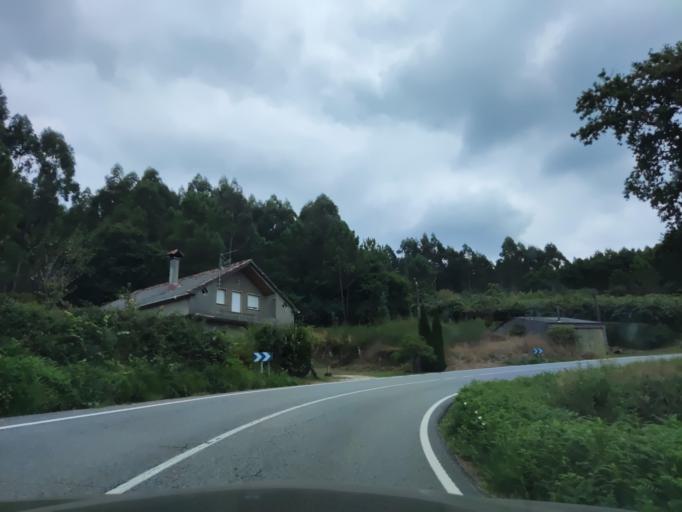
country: ES
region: Galicia
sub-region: Provincia da Coruna
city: Padron
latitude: 42.7402
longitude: -8.6323
